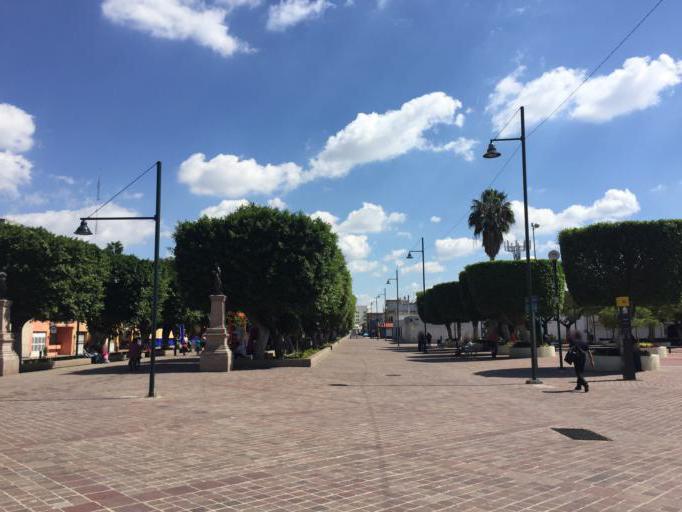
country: MX
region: Guanajuato
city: Leon
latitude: 21.1188
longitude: -101.6719
